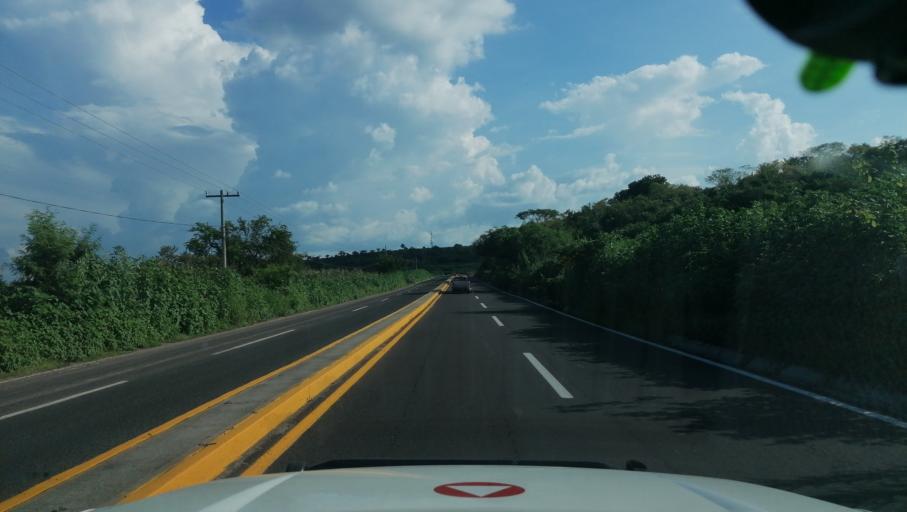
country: MX
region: Morelos
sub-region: Ayala
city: Abelardo L. Rodriguez
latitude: 18.7058
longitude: -98.9911
